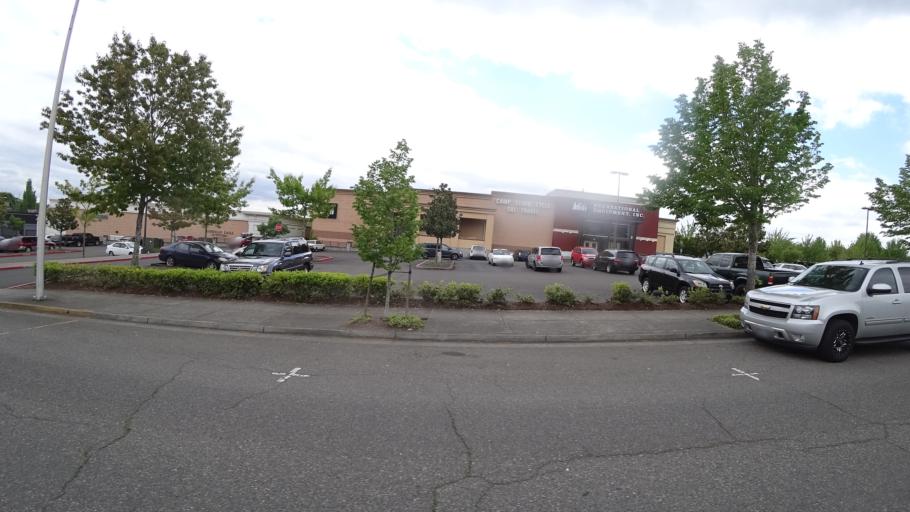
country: US
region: Oregon
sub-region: Washington County
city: Rockcreek
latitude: 45.5377
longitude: -122.8775
